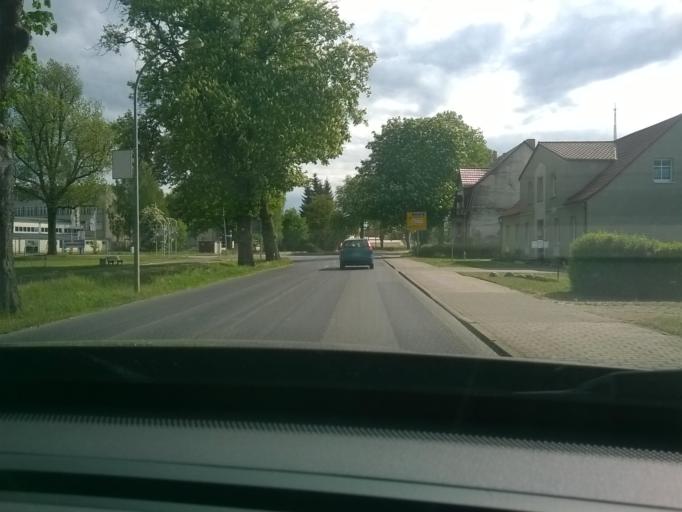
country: DE
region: Brandenburg
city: Wittstock
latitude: 53.1683
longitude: 12.4957
